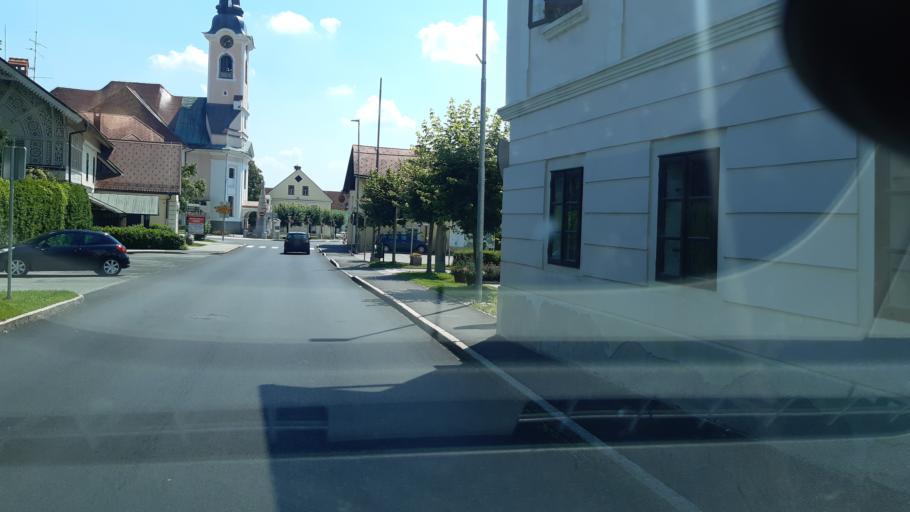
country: SI
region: Cerklje na Gorenjskem
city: Cerklje na Gorenjskem
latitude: 46.2540
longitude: 14.4872
